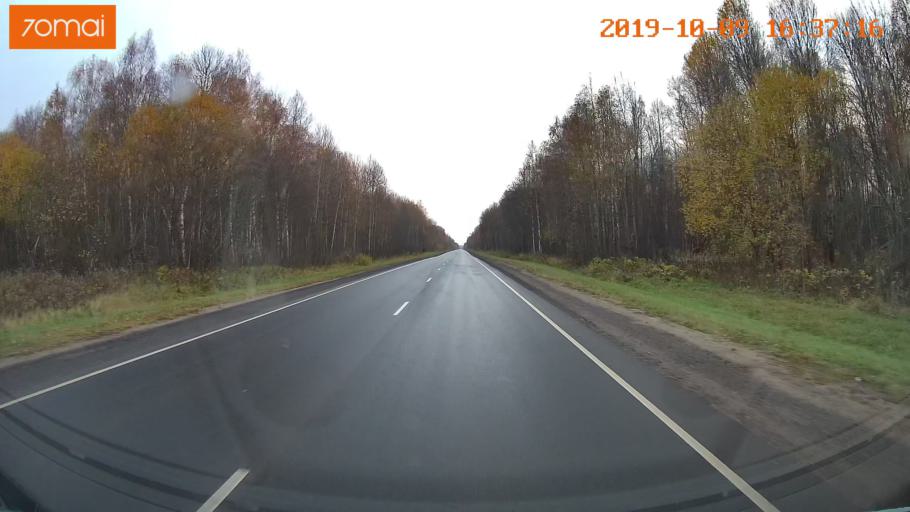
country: RU
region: Kostroma
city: Volgorechensk
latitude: 57.5296
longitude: 41.0224
